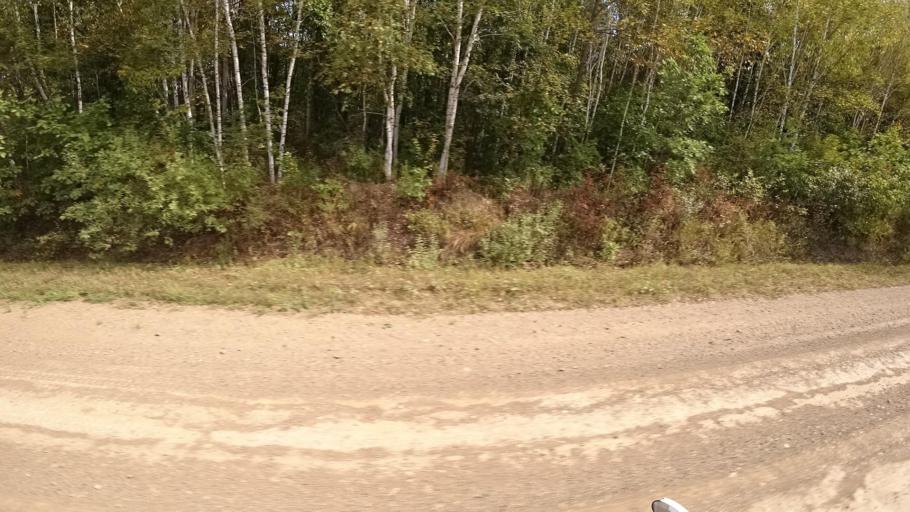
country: RU
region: Primorskiy
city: Yakovlevka
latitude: 44.7382
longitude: 133.6076
